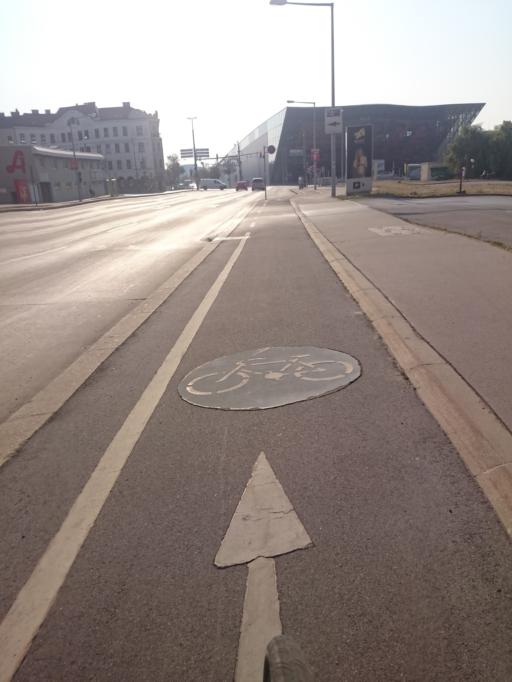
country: AT
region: Lower Austria
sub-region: Politischer Bezirk Korneuburg
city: Langenzersdorf
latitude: 48.2719
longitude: 16.4044
